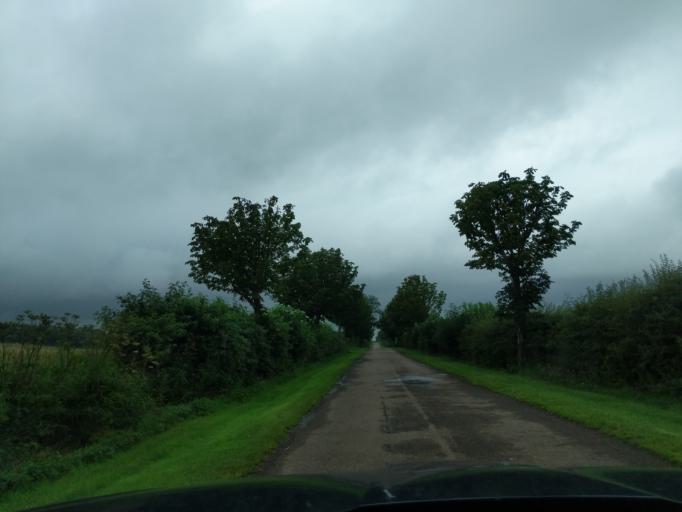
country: GB
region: England
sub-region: Northumberland
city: Ford
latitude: 55.6768
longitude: -2.1125
